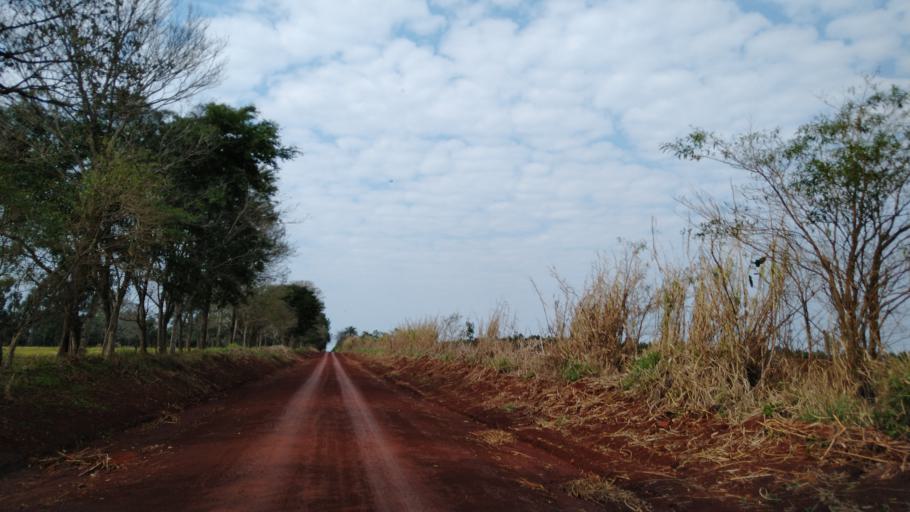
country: AR
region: Misiones
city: Capiovi
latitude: -26.9543
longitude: -55.0637
